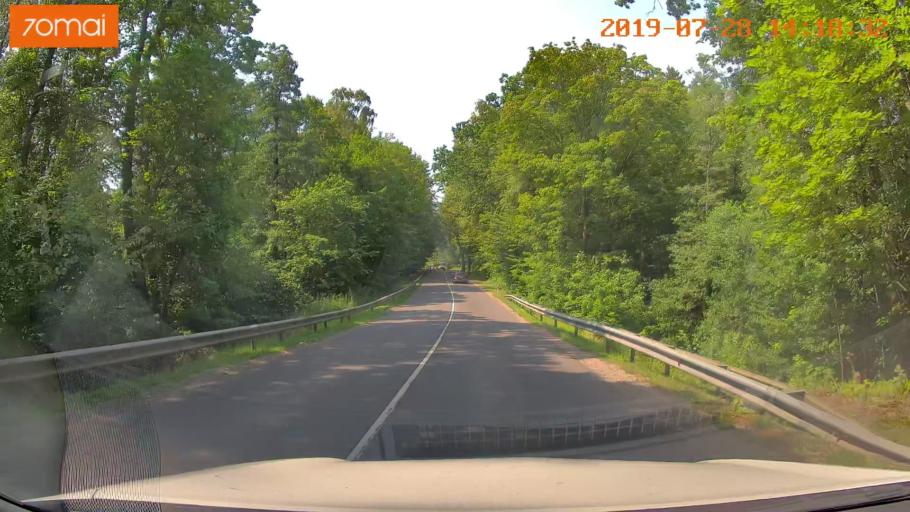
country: RU
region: Kaliningrad
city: Volochayevskoye
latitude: 54.8176
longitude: 20.2389
